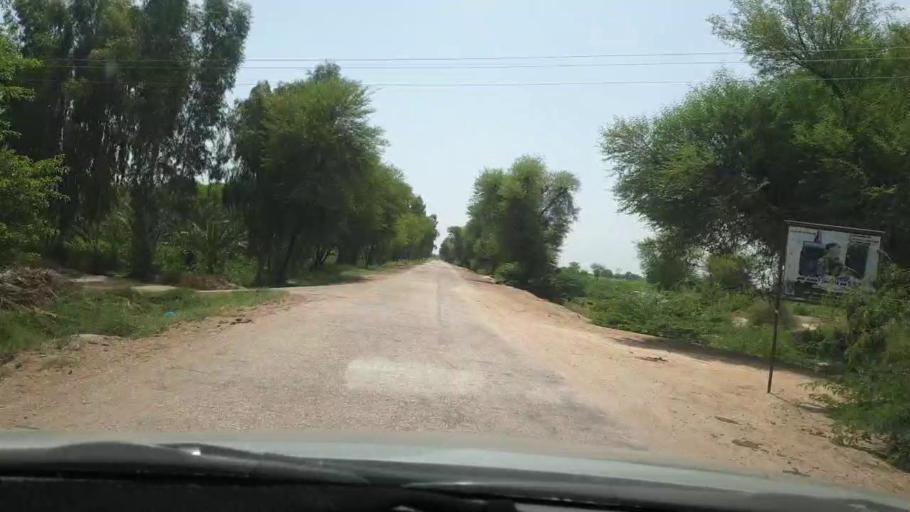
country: PK
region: Sindh
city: Pano Aqil
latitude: 27.7430
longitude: 69.2019
